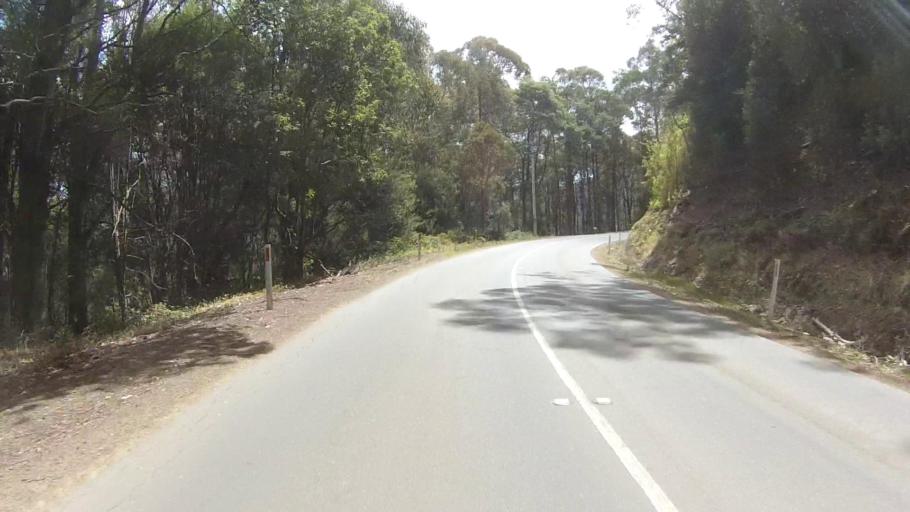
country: AU
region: Tasmania
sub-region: Kingborough
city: Kettering
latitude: -43.1279
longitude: 147.1677
